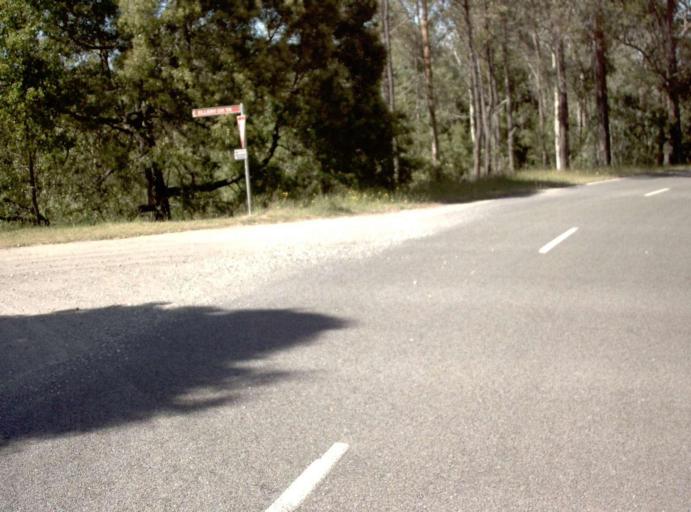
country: AU
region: New South Wales
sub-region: Bombala
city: Bombala
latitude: -37.3430
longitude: 148.6991
